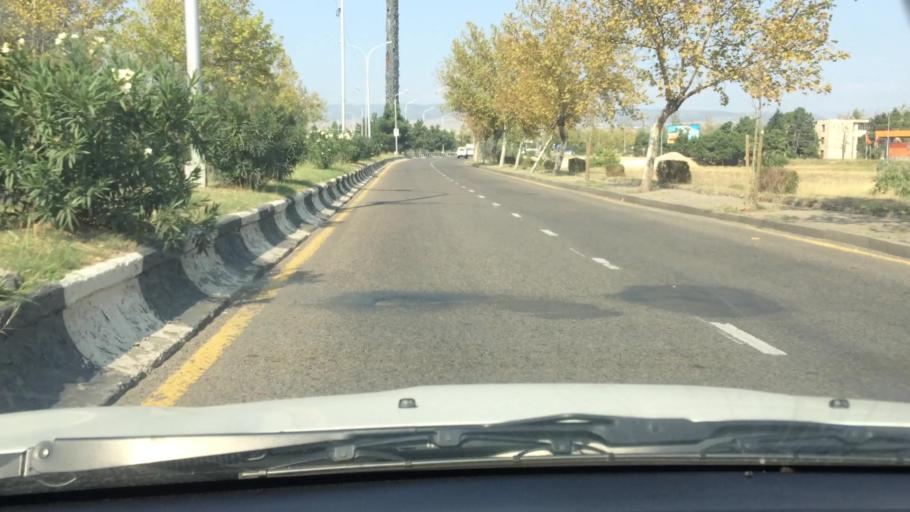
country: GE
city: Didi Lilo
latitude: 41.6889
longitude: 44.9531
